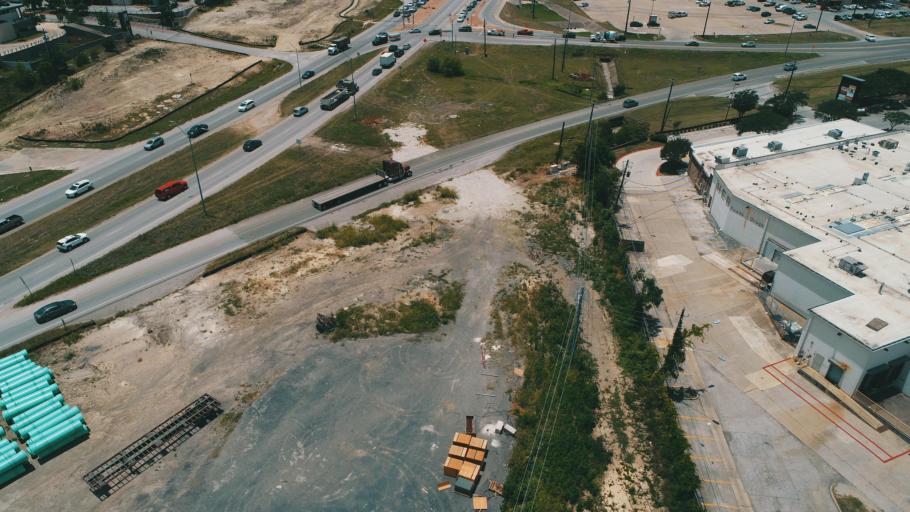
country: US
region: Texas
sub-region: Travis County
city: Barton Creek
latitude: 30.2347
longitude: -97.8729
